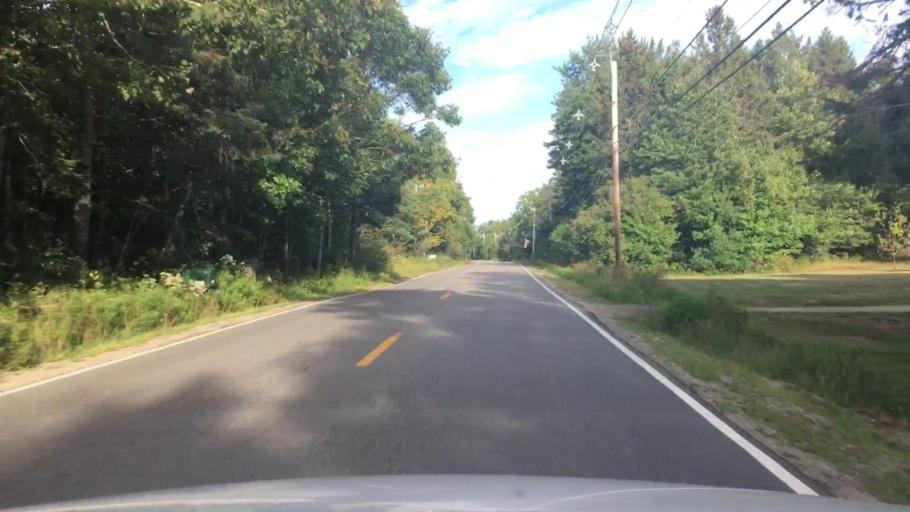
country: US
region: Maine
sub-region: Hancock County
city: Trenton
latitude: 44.4375
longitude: -68.3847
